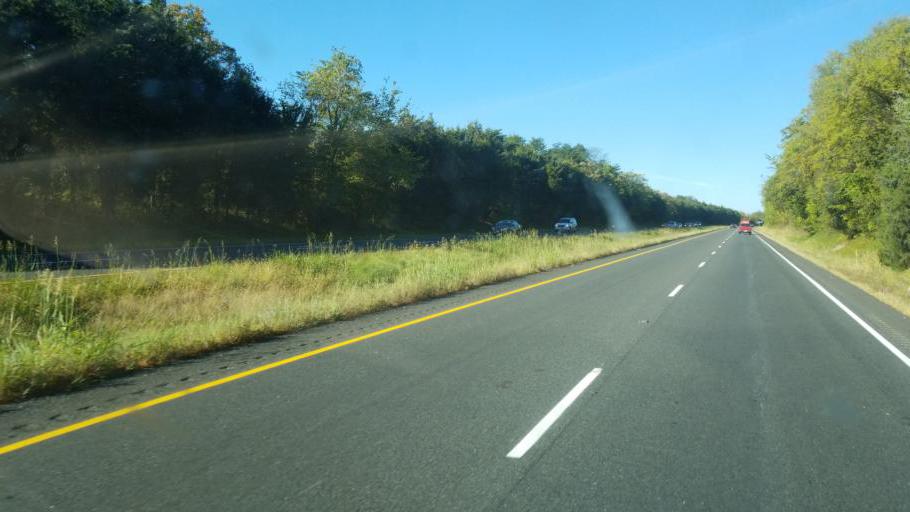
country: US
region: Virginia
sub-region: Culpeper County
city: Culpeper
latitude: 38.5050
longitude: -77.8823
